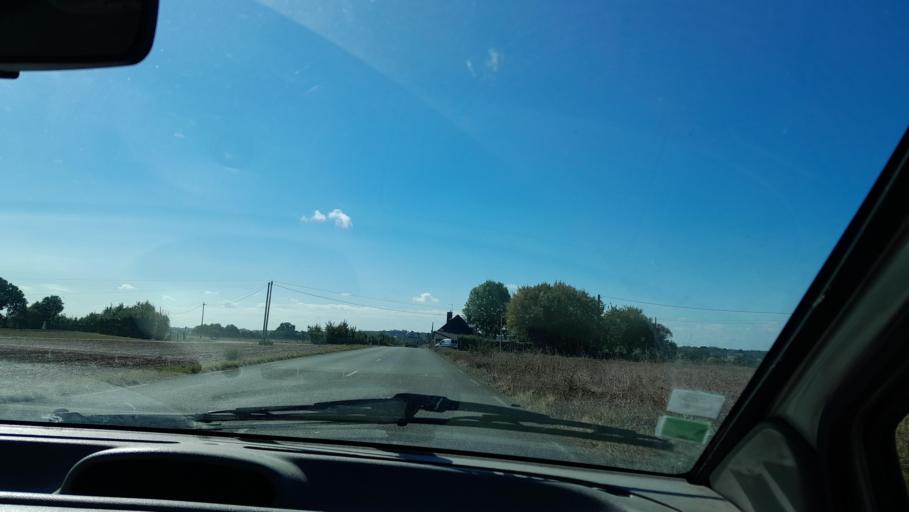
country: FR
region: Pays de la Loire
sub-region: Departement de la Mayenne
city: Ballots
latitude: 47.9082
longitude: -1.0570
